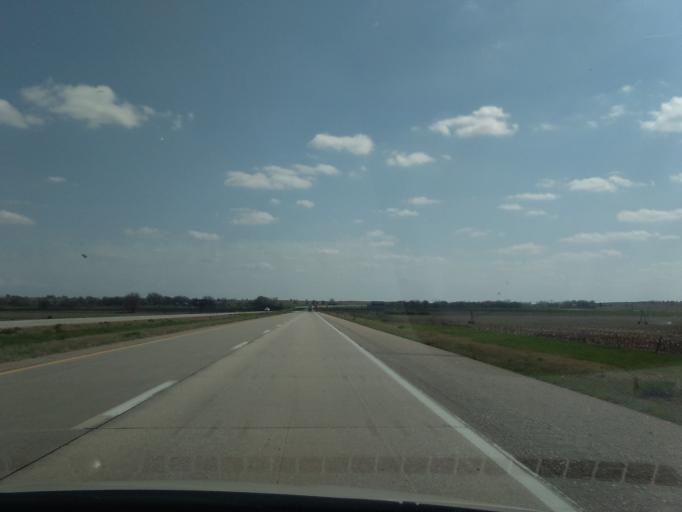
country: US
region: Nebraska
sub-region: Thayer County
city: Hebron
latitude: 40.1580
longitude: -97.5709
